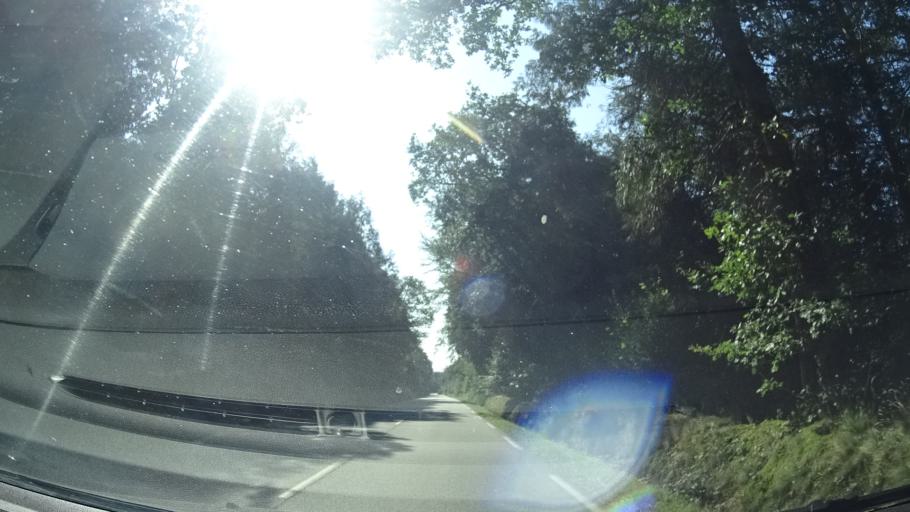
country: FR
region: Brittany
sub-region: Departement du Finistere
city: Cast
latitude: 48.1752
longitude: -4.1244
